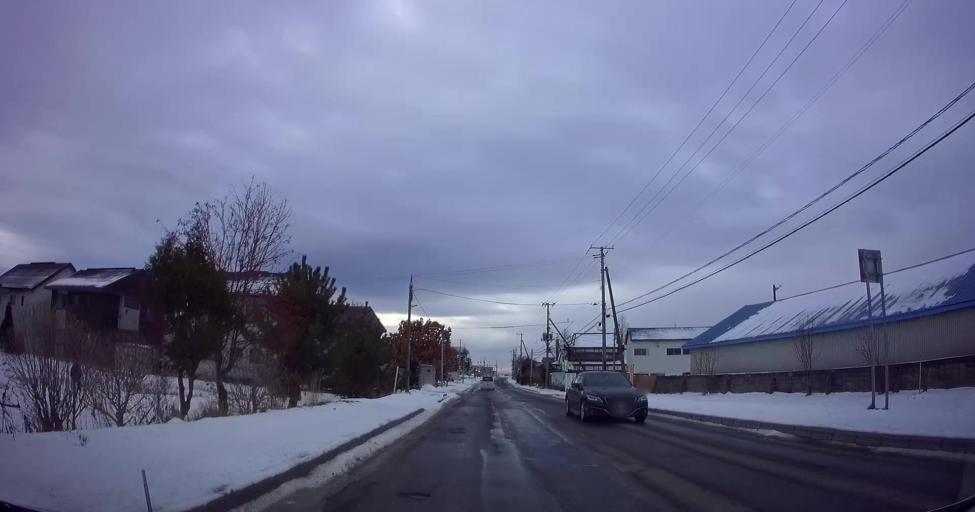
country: JP
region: Hokkaido
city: Kamiiso
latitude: 41.8253
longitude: 140.6855
